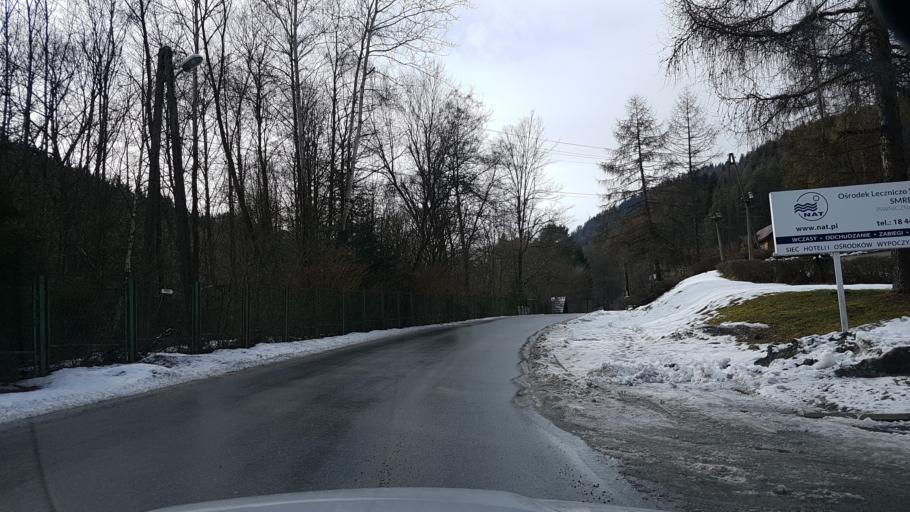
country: PL
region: Lesser Poland Voivodeship
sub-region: Powiat nowosadecki
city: Piwniczna-Zdroj
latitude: 49.4317
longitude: 20.6785
